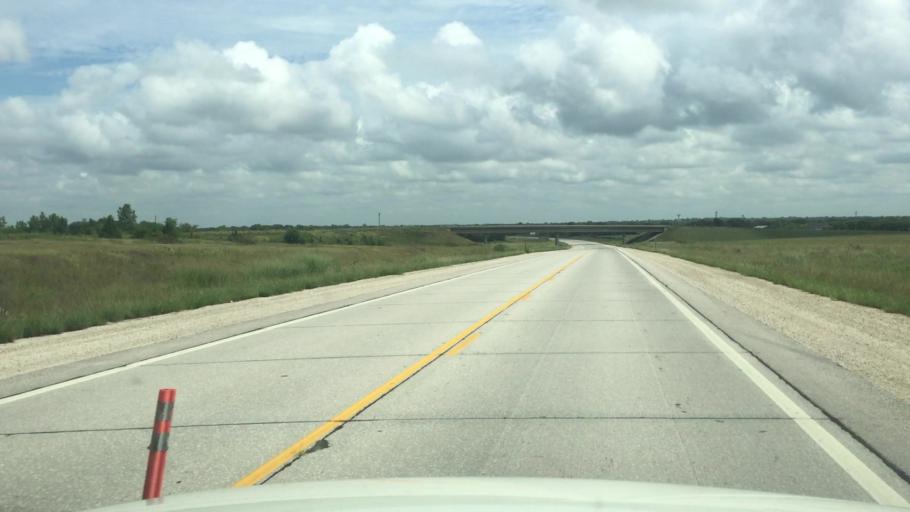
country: US
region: Kansas
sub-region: Allen County
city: Iola
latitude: 37.8900
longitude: -95.3885
